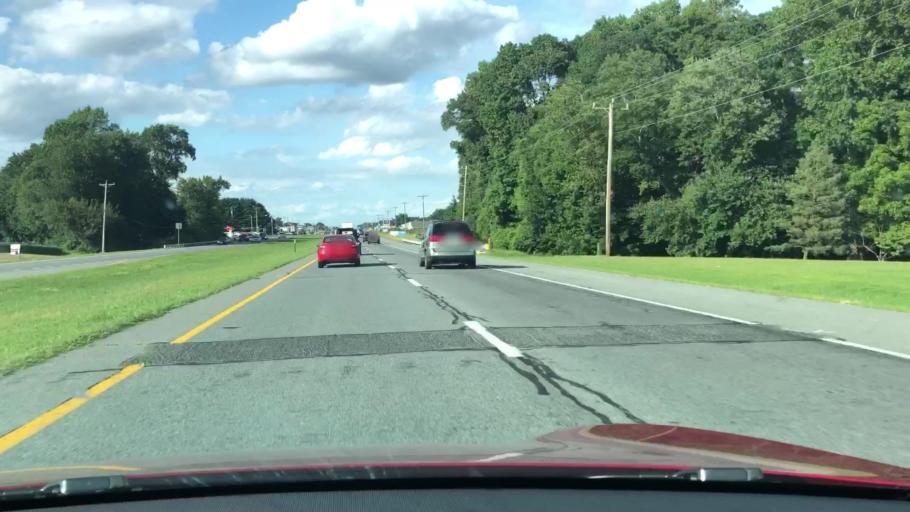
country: US
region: Delaware
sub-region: Kent County
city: Camden
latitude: 39.0898
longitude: -75.5482
